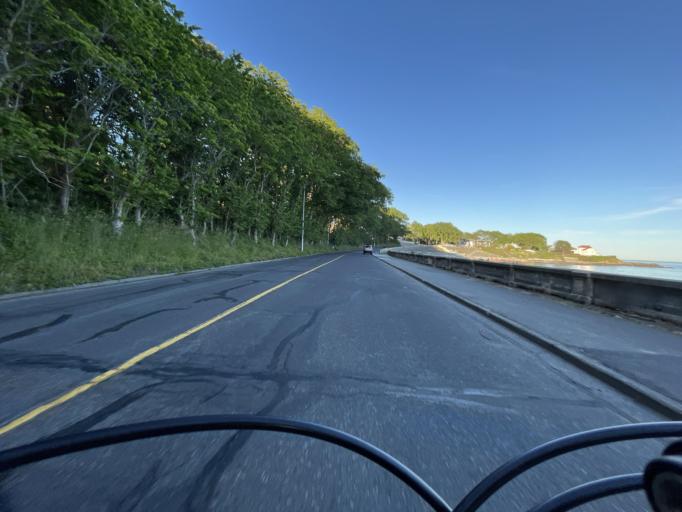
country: CA
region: British Columbia
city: Victoria
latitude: 48.4103
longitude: -123.3394
